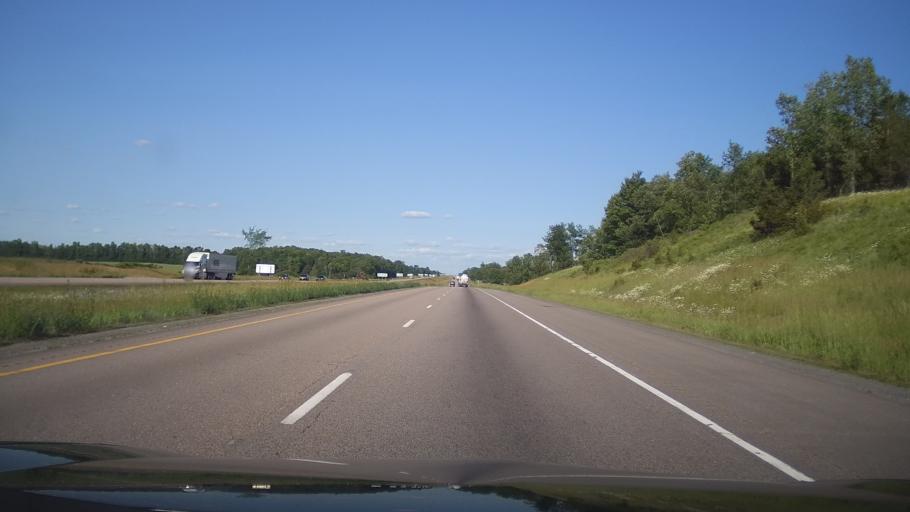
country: CA
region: Ontario
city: Deseronto
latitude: 44.2396
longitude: -77.0976
